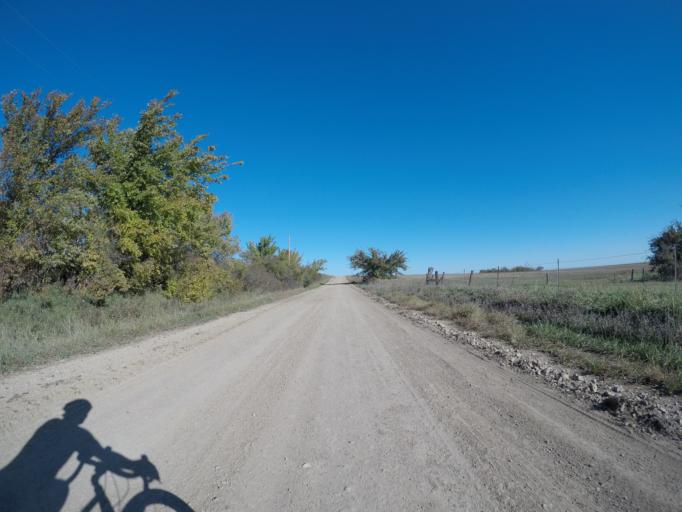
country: US
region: Kansas
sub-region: Wabaunsee County
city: Alma
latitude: 38.8619
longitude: -96.4098
